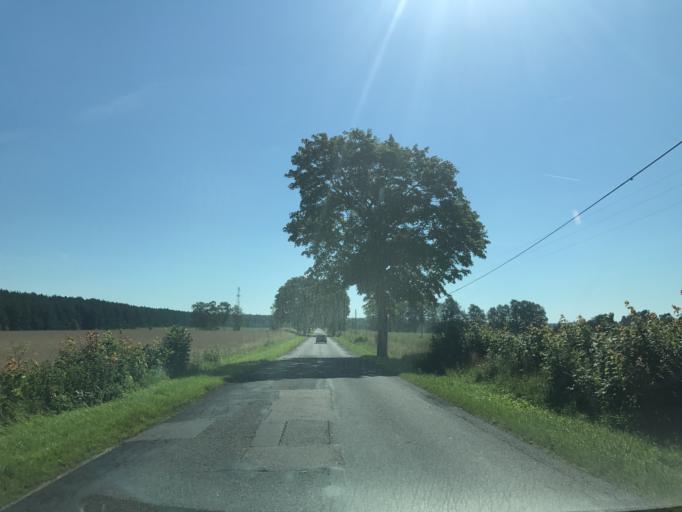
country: PL
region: Pomeranian Voivodeship
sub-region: Powiat bytowski
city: Czarna Dabrowka
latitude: 54.3614
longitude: 17.5296
